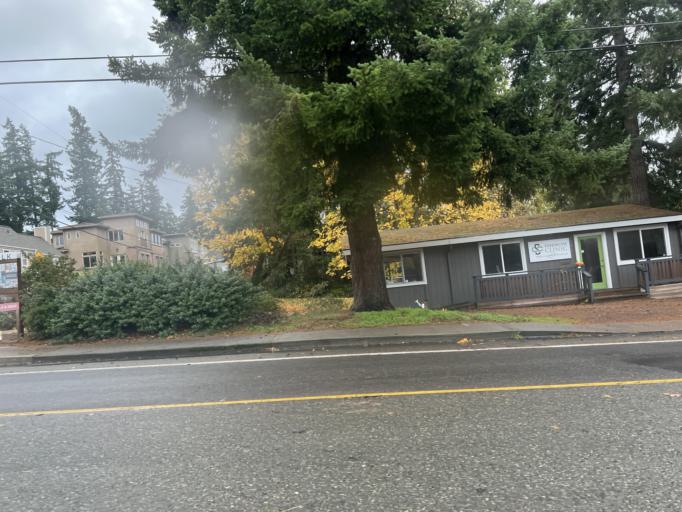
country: US
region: Washington
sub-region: Kitsap County
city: Bainbridge Island
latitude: 47.6277
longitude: -122.5210
